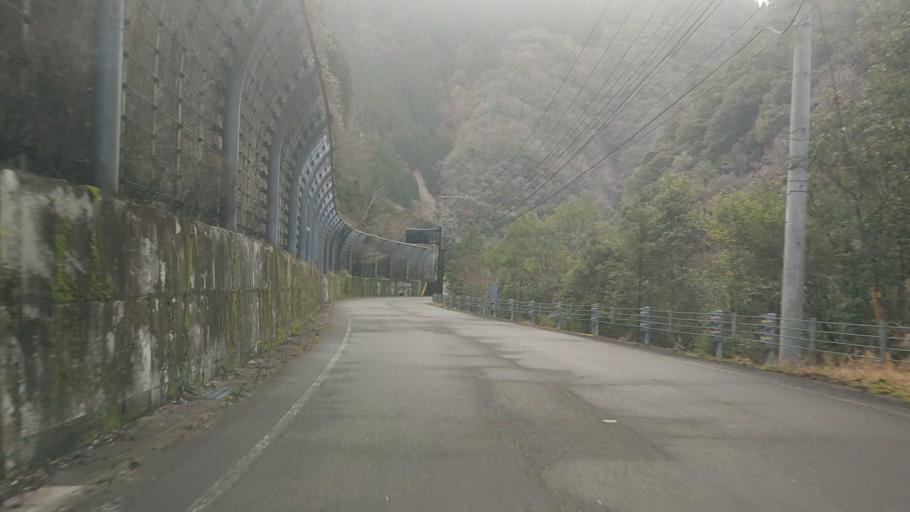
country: JP
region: Kumamoto
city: Matsubase
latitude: 32.4789
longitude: 130.8880
